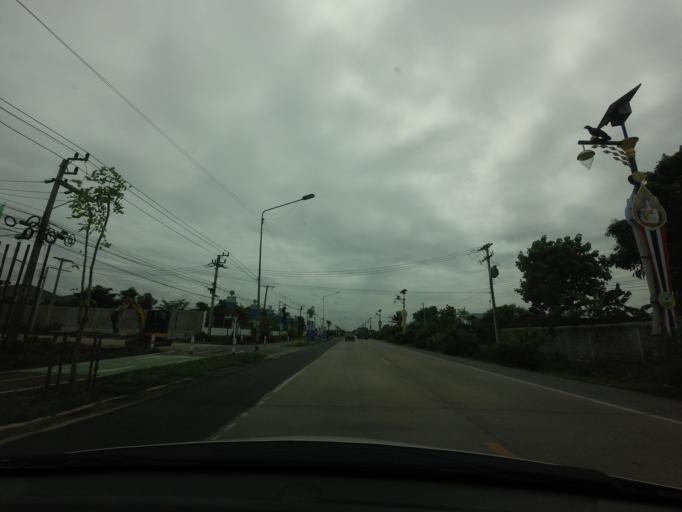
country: TH
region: Pathum Thani
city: Lam Luk Ka
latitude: 13.9300
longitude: 100.7342
